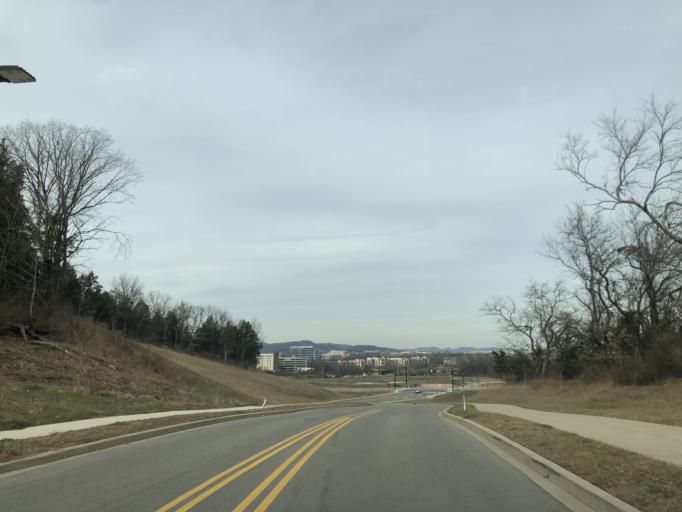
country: US
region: Tennessee
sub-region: Williamson County
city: Franklin
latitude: 35.9262
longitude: -86.8111
